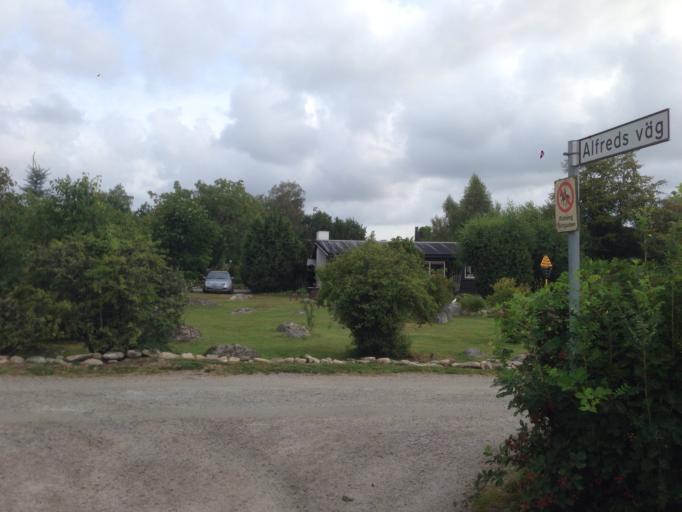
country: SE
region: Blekinge
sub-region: Karlshamns Kommun
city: Morrum
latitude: 56.1105
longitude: 14.6880
